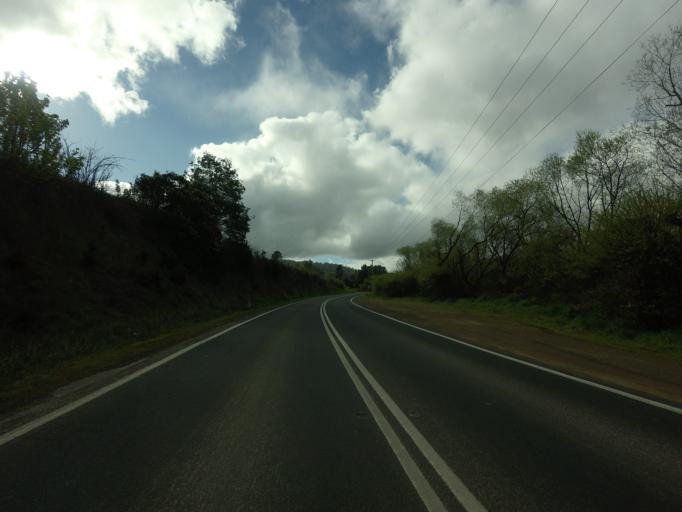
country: AU
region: Tasmania
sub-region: Huon Valley
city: Franklin
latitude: -43.0757
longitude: 147.0164
